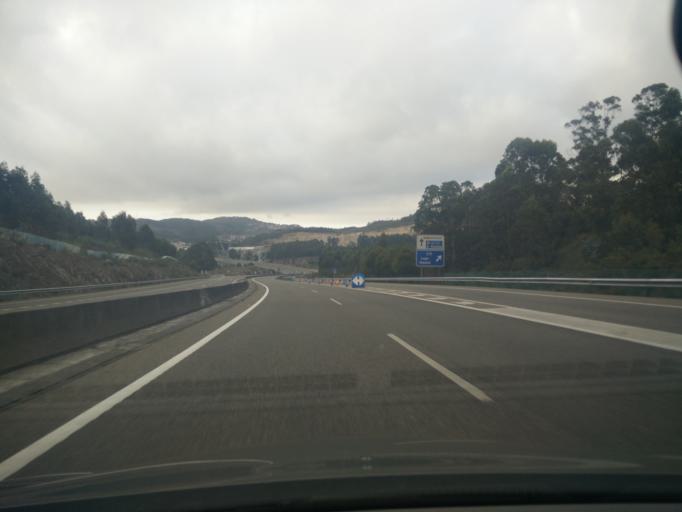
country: ES
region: Galicia
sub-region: Provincia da Coruna
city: Arteixo
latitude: 43.3012
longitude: -8.4760
